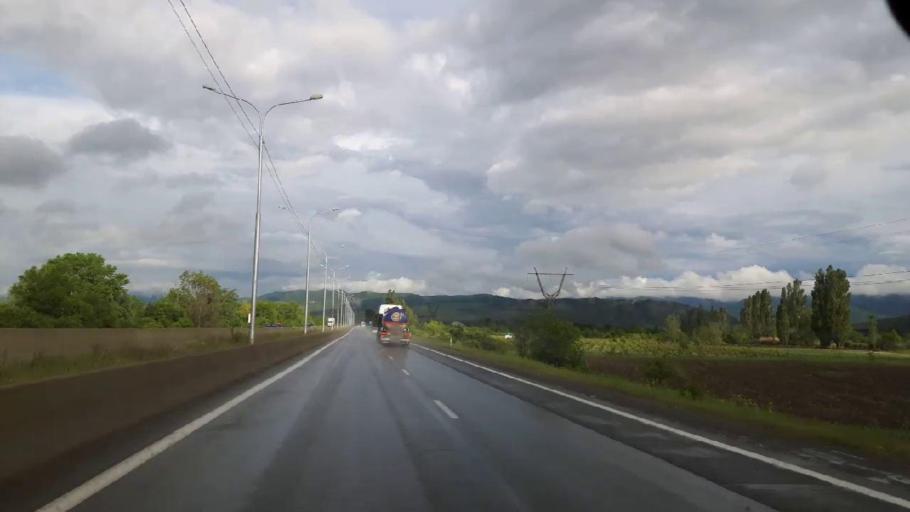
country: GE
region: Shida Kartli
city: Kaspi
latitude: 41.9226
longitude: 44.5442
